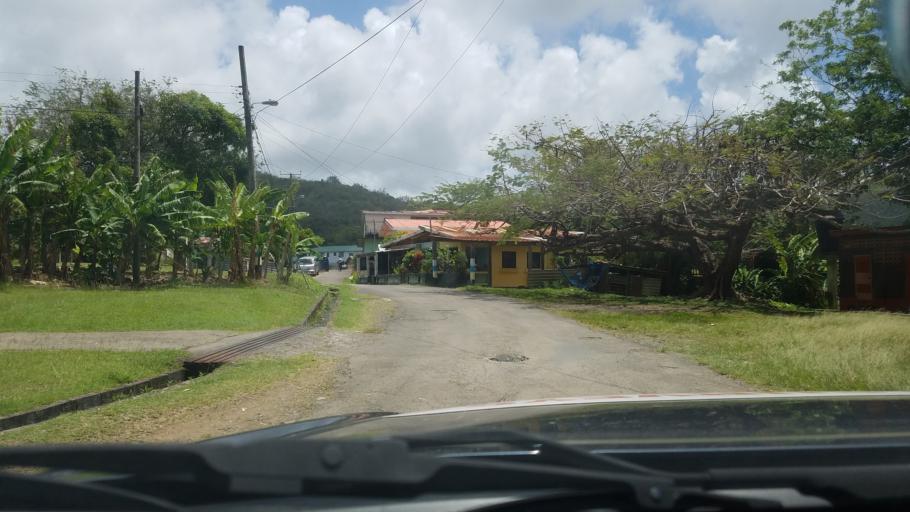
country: LC
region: Gros-Islet
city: Gros Islet
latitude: 14.0545
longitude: -60.9298
